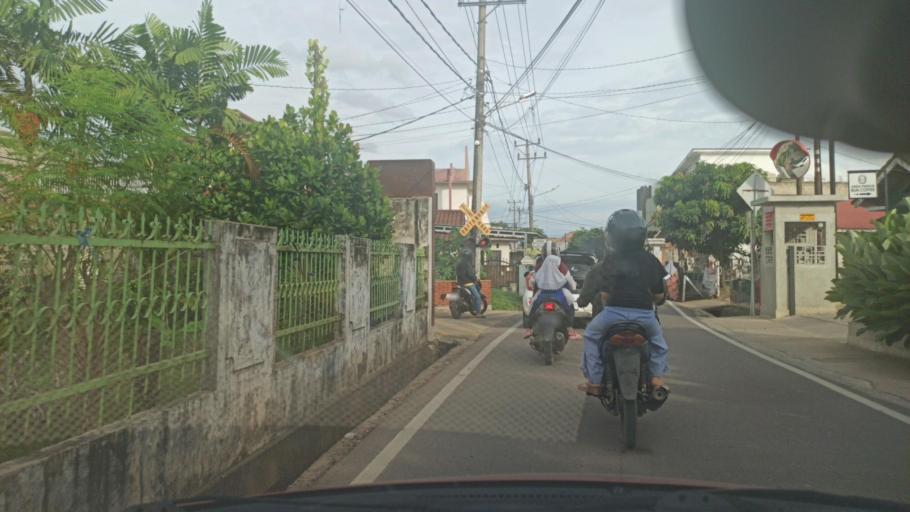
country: ID
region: South Sumatra
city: Palembang
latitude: -2.9811
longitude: 104.7196
